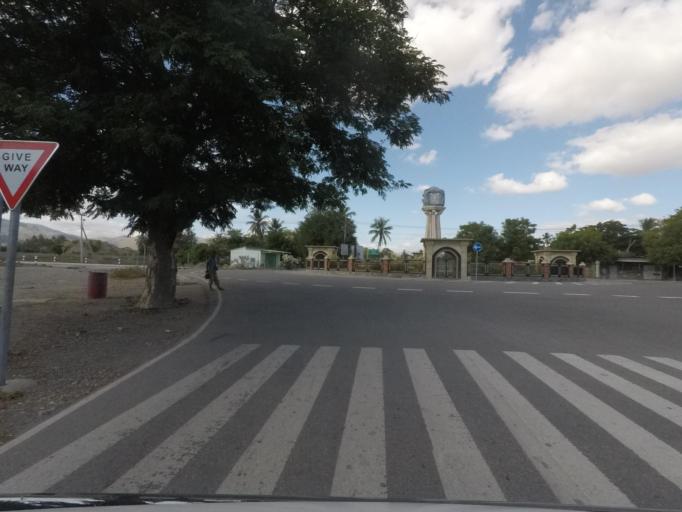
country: TL
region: Manatuto
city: Manatuto
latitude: -8.5181
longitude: 126.0074
